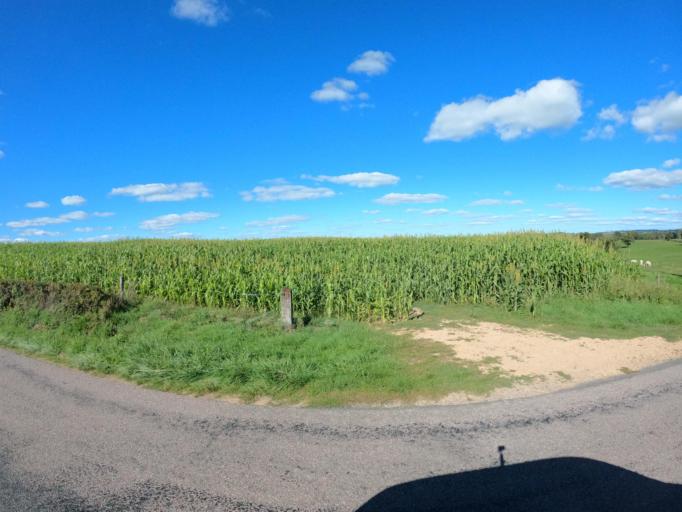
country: FR
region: Auvergne
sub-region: Departement de l'Allier
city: Buxieres-les-Mines
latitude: 46.4029
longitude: 2.9871
